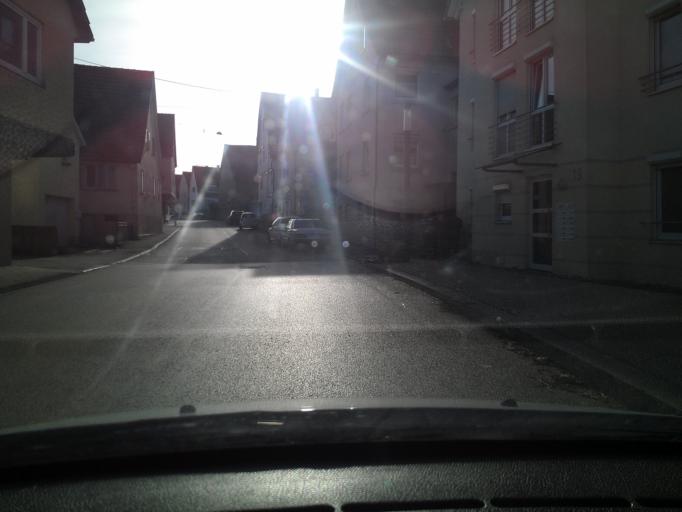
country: DE
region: Baden-Wuerttemberg
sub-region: Regierungsbezirk Stuttgart
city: Neuhausen auf den Fildern
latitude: 48.6864
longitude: 9.2784
